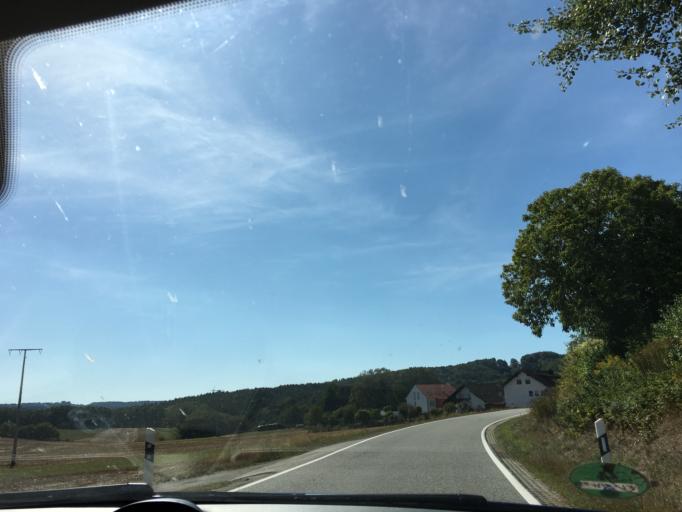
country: DE
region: Rheinland-Pfalz
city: Krickenbach
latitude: 49.3630
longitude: 7.6789
